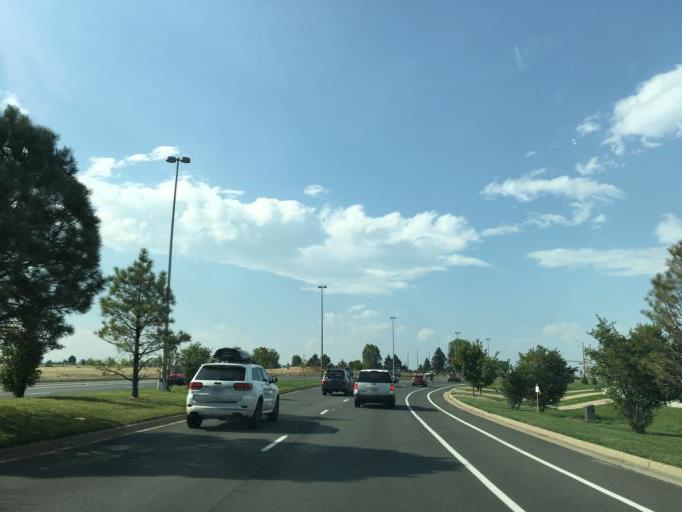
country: US
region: Colorado
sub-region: Boulder County
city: Louisville
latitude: 39.9385
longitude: -105.1271
